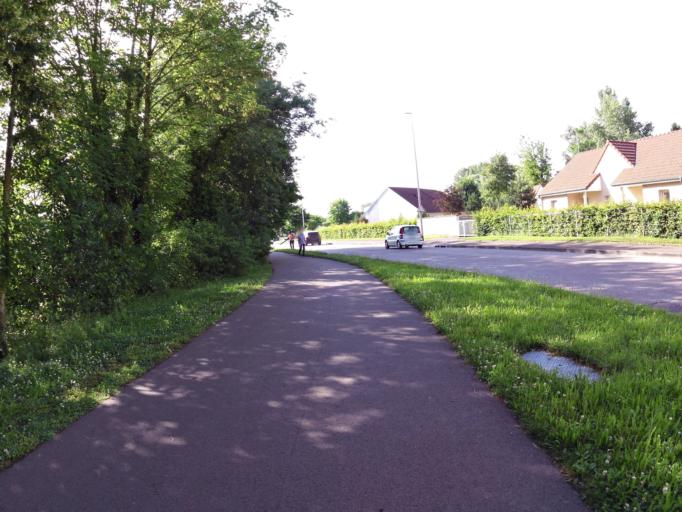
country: FR
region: Champagne-Ardenne
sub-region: Departement de l'Aube
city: Saint-Julien-les-Villas
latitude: 48.2821
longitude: 4.0934
